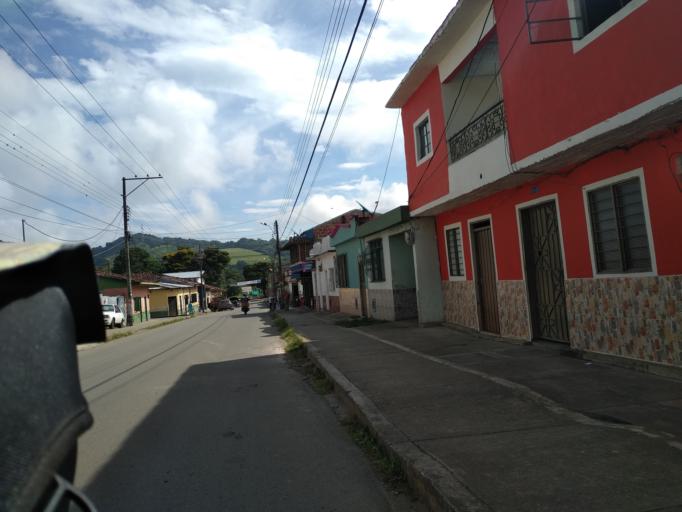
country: CO
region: Valle del Cauca
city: Caicedonia
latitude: 4.3381
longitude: -75.8290
